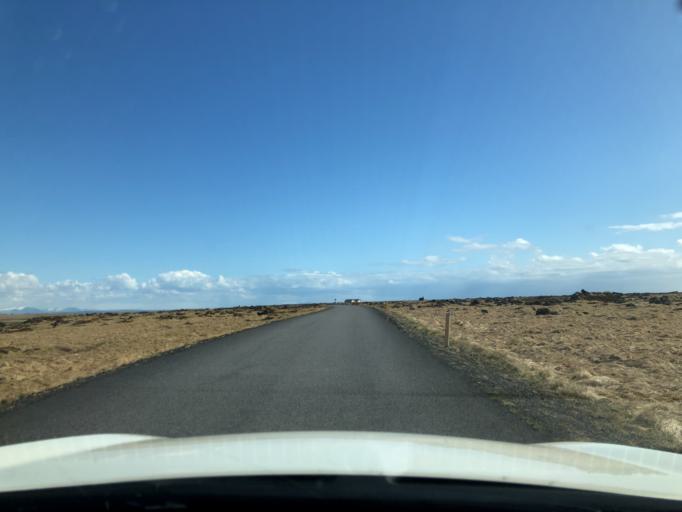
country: IS
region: West
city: Olafsvik
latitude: 64.8278
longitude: -23.4019
